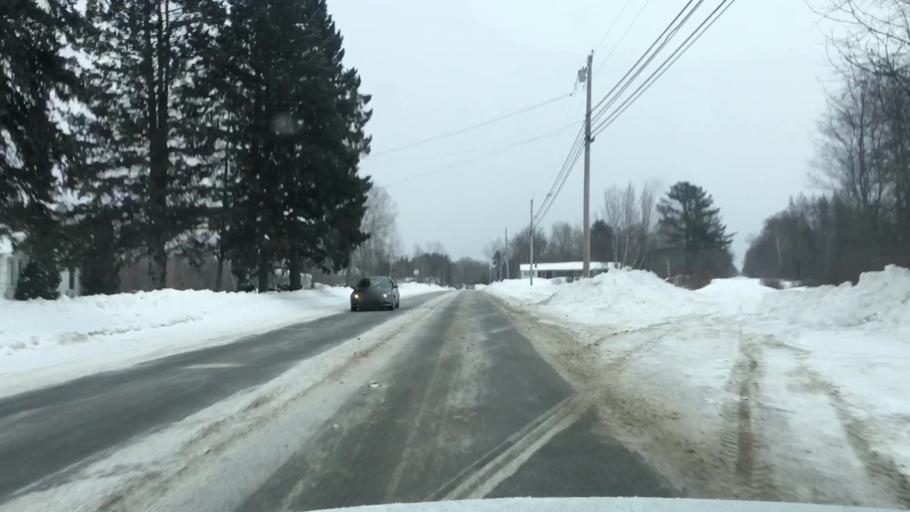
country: US
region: Maine
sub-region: Penobscot County
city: Lincoln
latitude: 45.3975
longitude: -68.4921
